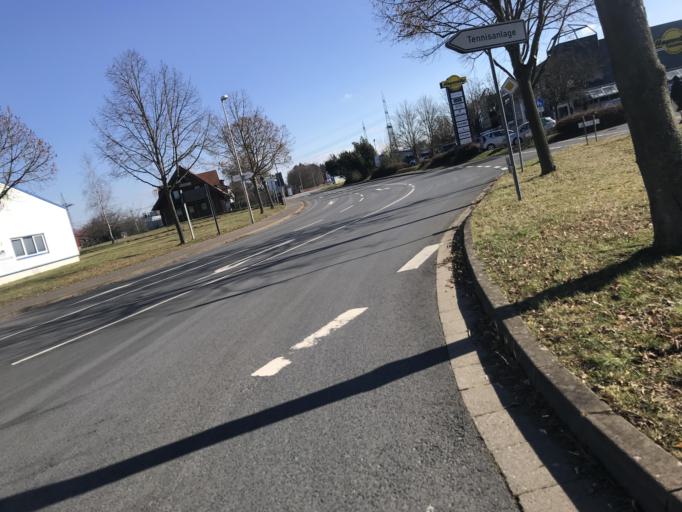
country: DE
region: Hesse
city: Schwalmstadt
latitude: 50.9102
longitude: 9.1987
